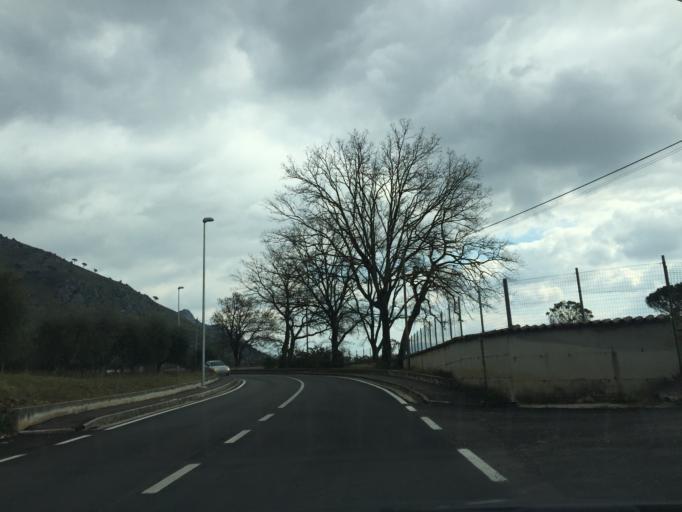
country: IT
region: Latium
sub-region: Provincia di Frosinone
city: Villa Santa Lucia
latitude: 41.4952
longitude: 13.7718
